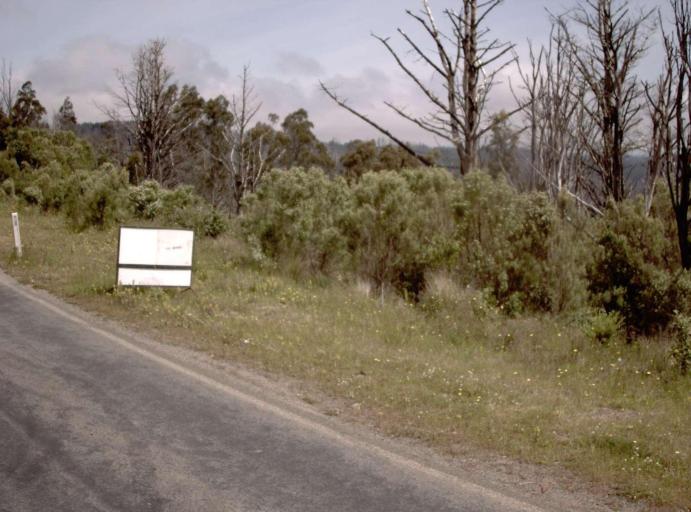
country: AU
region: Victoria
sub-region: Latrobe
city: Traralgon
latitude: -38.3975
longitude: 146.5594
